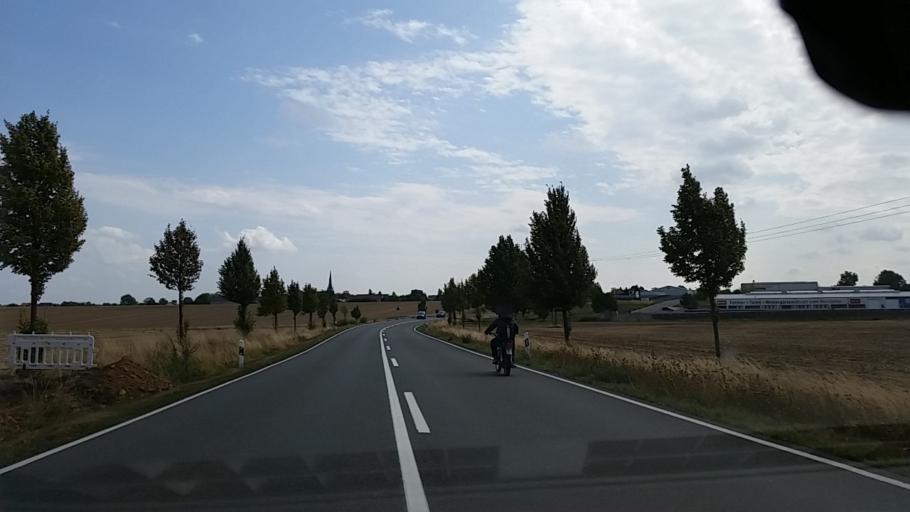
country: DE
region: Saxony-Anhalt
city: Nemsdorf-Gohrendorf
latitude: 51.3518
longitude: 11.6340
